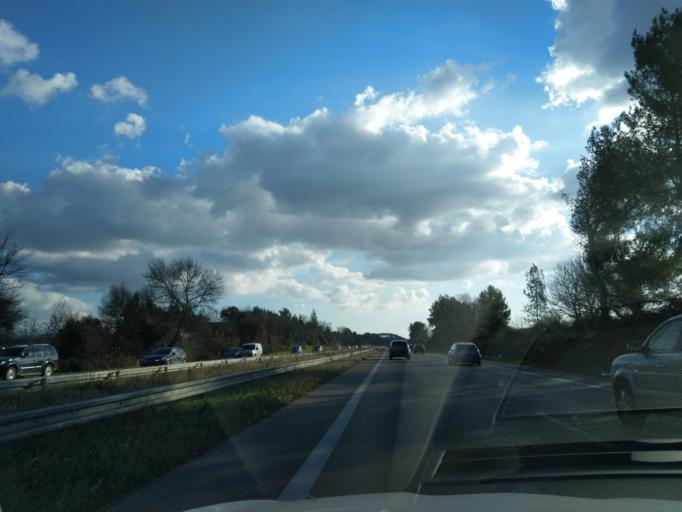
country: FR
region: Provence-Alpes-Cote d'Azur
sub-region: Departement des Bouches-du-Rhone
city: Bouc-Bel-Air
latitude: 43.4861
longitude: 5.4078
